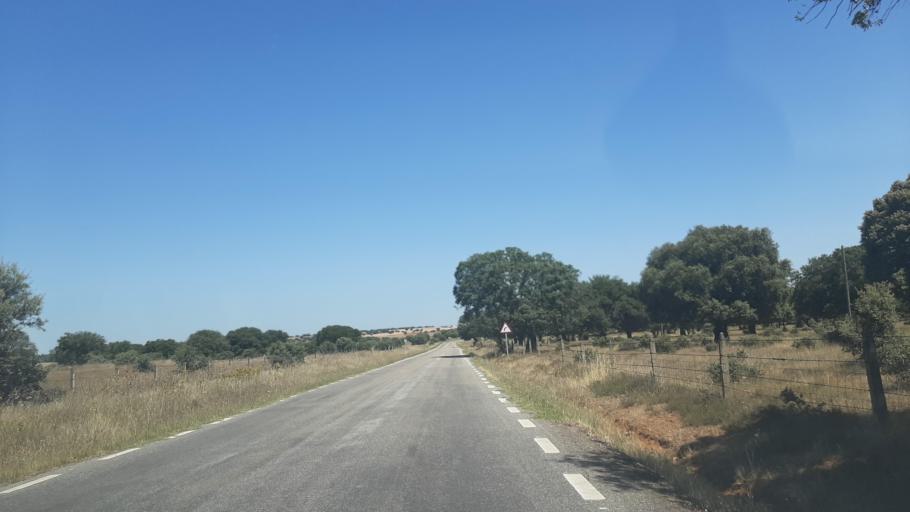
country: ES
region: Castille and Leon
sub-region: Provincia de Salamanca
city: Cabrillas
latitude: 40.7282
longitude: -6.1765
